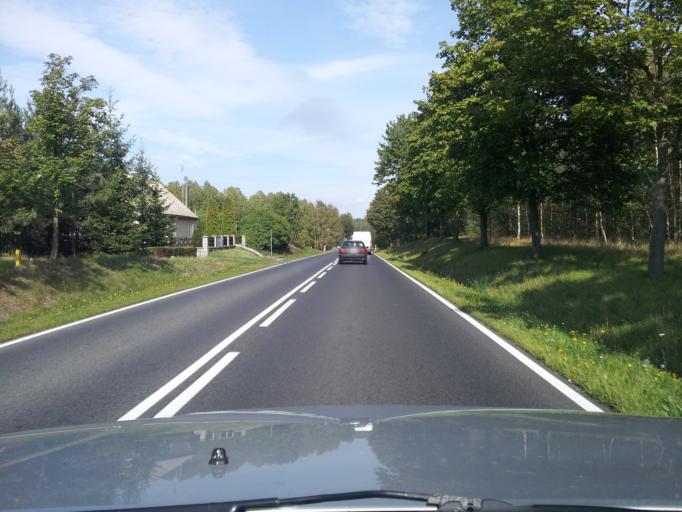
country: PL
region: Warmian-Masurian Voivodeship
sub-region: Powiat nowomiejski
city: Nowe Miasto Lubawskie
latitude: 53.4664
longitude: 19.6183
